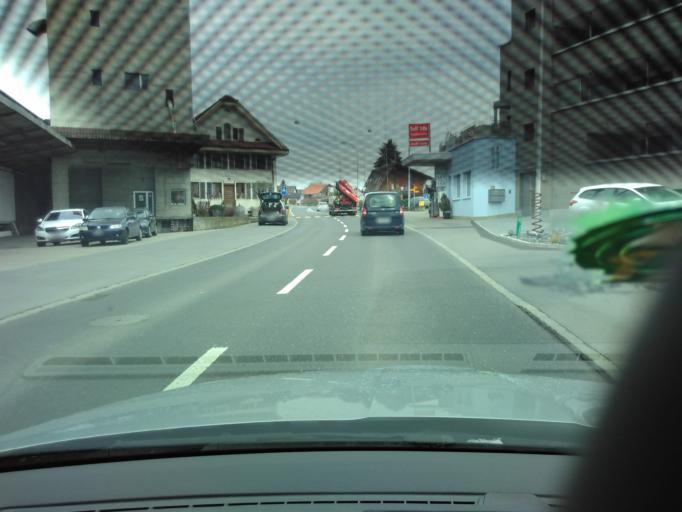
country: CH
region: Lucerne
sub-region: Hochdorf District
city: Hitzkirch
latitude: 47.2131
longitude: 8.2660
